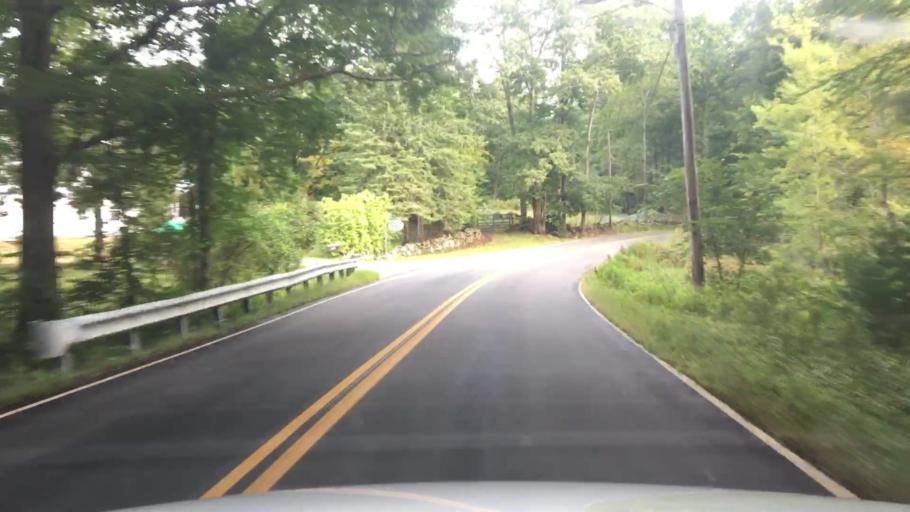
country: US
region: Maine
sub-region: York County
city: York Harbor
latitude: 43.1145
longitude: -70.6696
